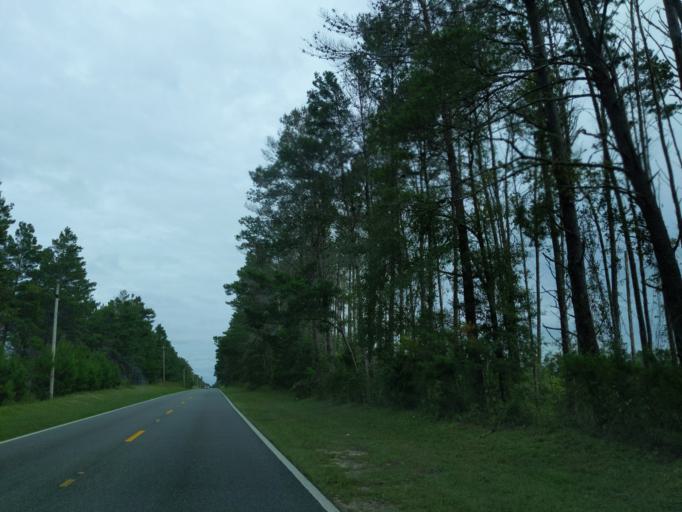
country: US
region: Florida
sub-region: Leon County
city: Woodville
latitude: 30.3754
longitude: -84.2133
